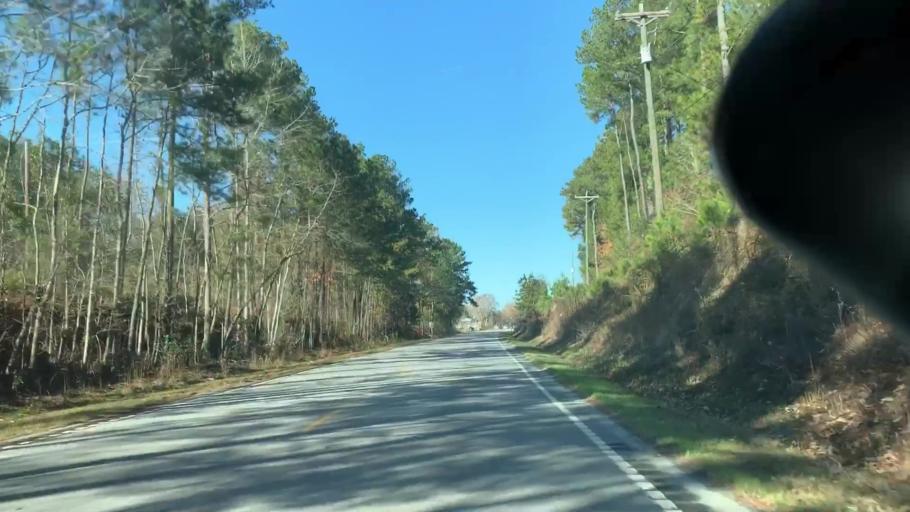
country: US
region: South Carolina
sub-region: Richland County
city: Hopkins
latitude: 33.9247
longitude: -80.9597
